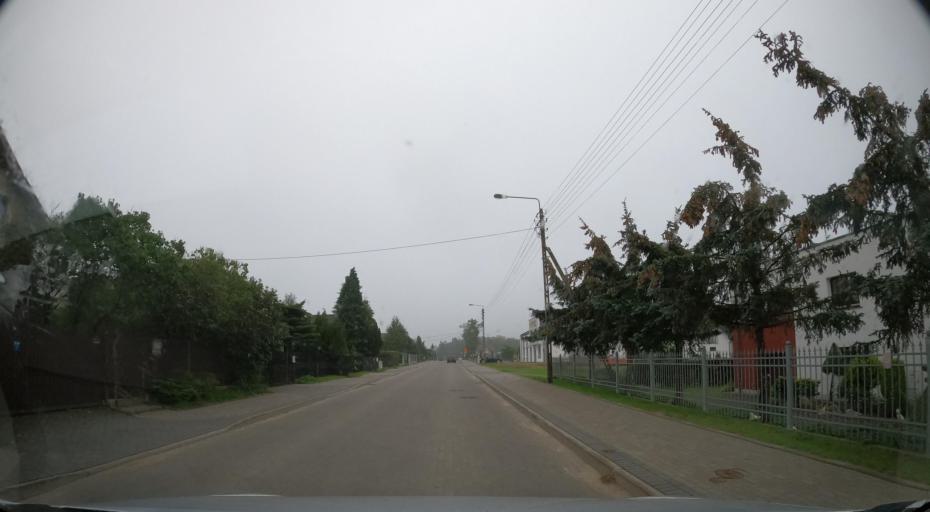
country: PL
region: Pomeranian Voivodeship
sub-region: Powiat kartuski
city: Chwaszczyno
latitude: 54.4414
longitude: 18.4188
